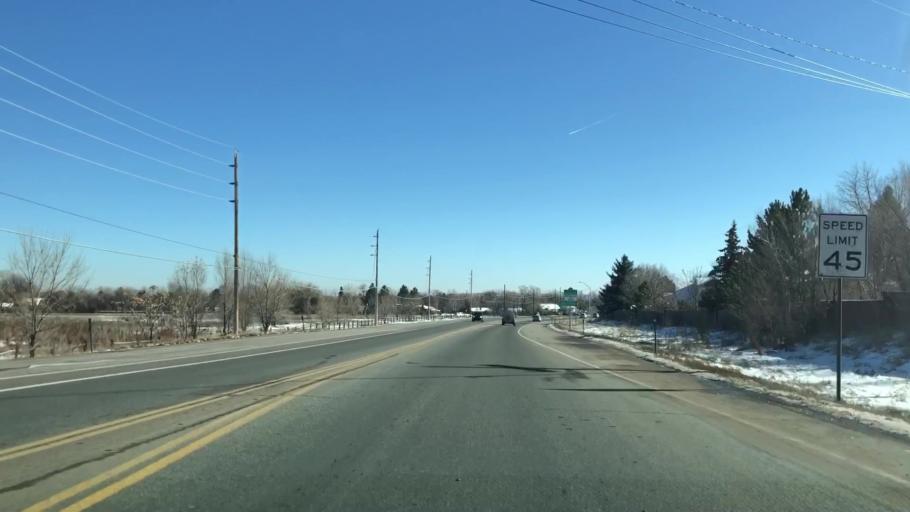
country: US
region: Colorado
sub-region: Boulder County
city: Boulder
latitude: 40.0535
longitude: -105.2634
